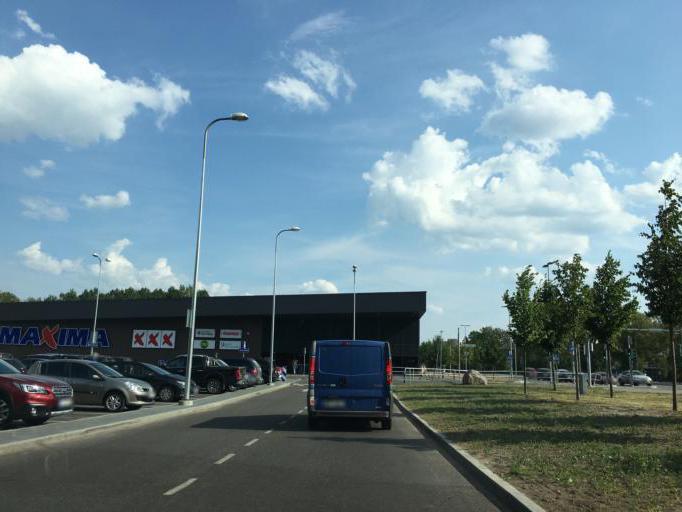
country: EE
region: Harju
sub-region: Saue vald
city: Laagri
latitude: 59.4217
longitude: 24.6497
